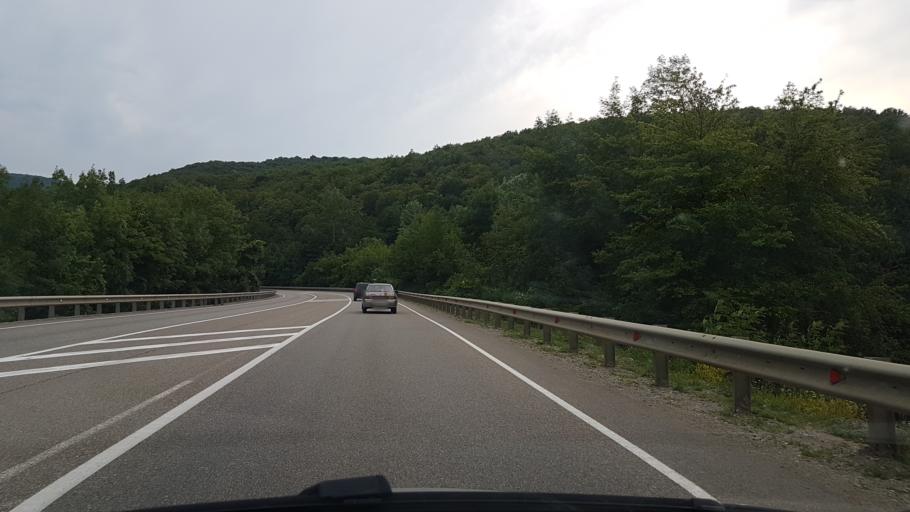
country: RU
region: Krasnodarskiy
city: Goryachiy Klyuch
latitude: 44.6146
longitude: 39.0831
